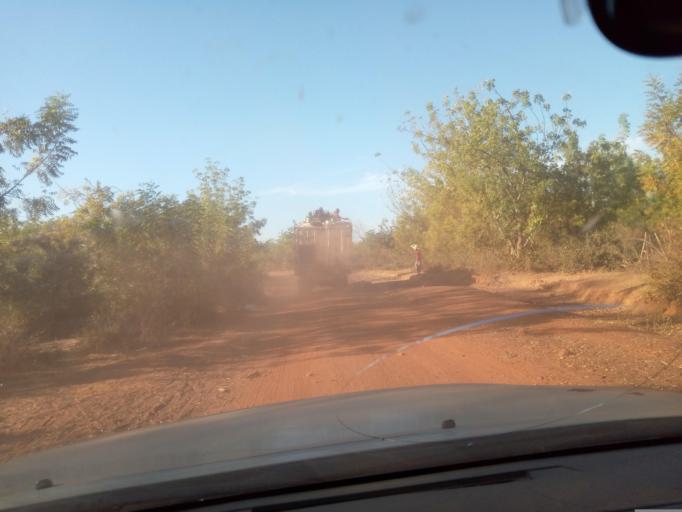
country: ML
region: Sikasso
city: Sikasso
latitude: 11.4811
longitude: -5.4787
